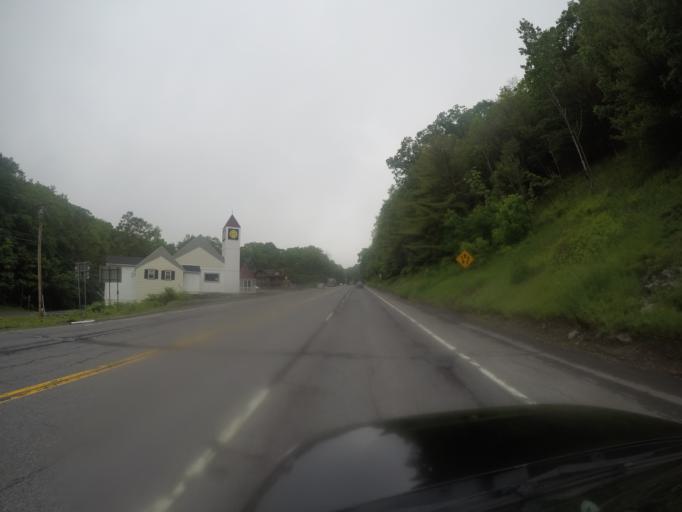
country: US
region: New York
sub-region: Ulster County
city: West Hurley
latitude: 41.9703
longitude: -74.0722
